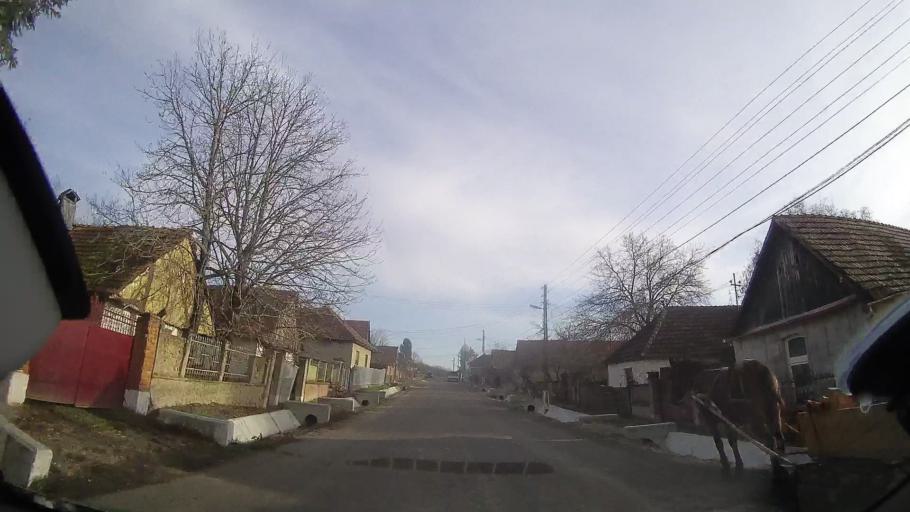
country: RO
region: Bihor
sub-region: Comuna Sarbi
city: Sarbi
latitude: 47.1777
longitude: 22.1457
